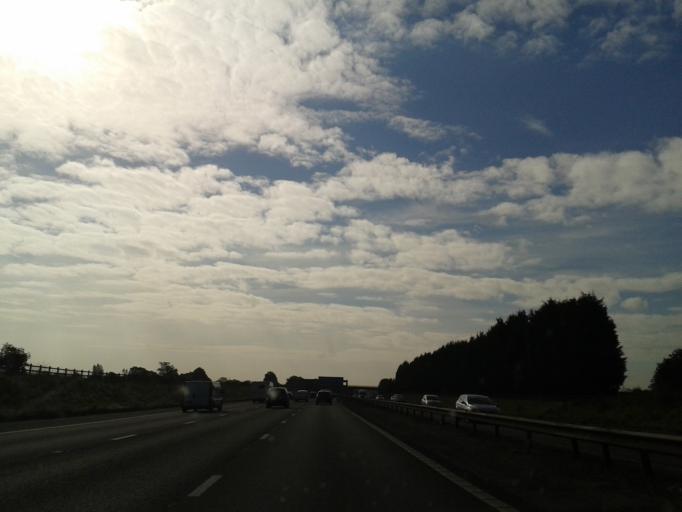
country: GB
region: England
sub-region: Cheshire East
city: Holmes Chapel
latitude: 53.2167
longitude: -2.3894
